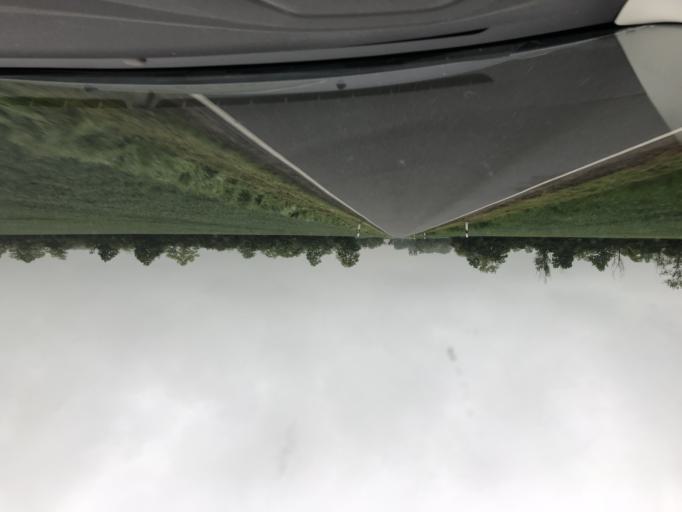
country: DE
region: Saxony
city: Jesewitz
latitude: 51.4343
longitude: 12.5344
